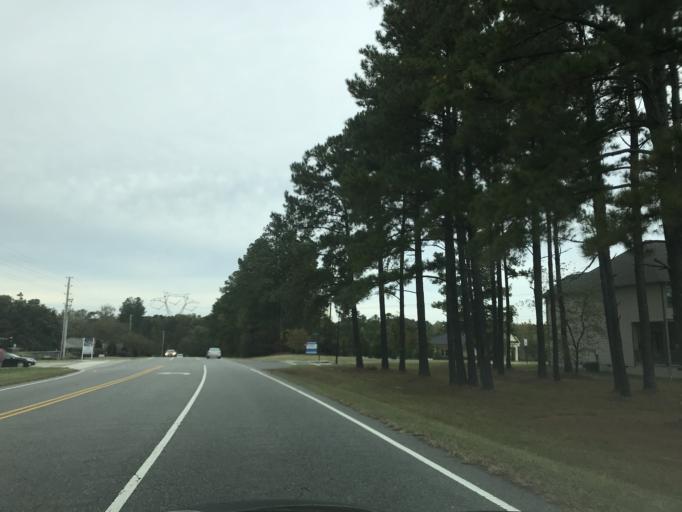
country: US
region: North Carolina
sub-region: Wake County
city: Rolesville
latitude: 35.9121
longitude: -78.5048
